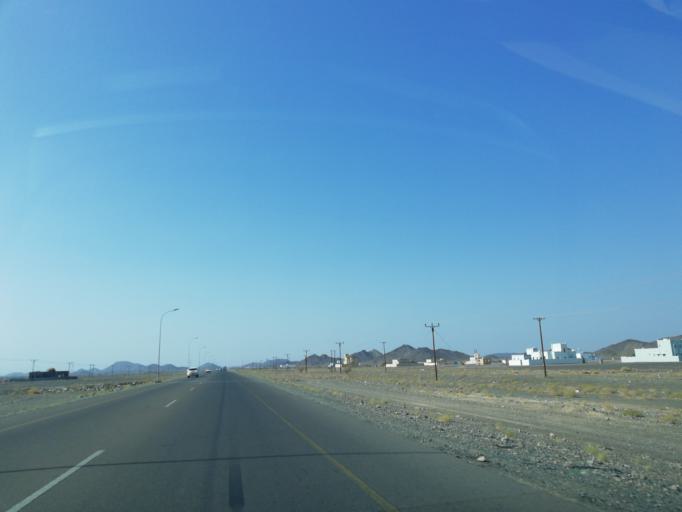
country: OM
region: Ash Sharqiyah
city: Ibra'
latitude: 22.7650
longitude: 58.1451
